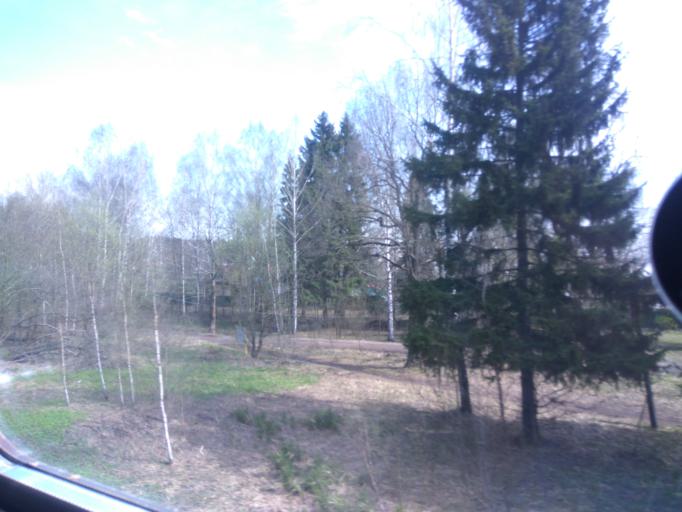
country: RU
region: Moskovskaya
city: Lugovaya
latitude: 56.0524
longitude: 37.4920
